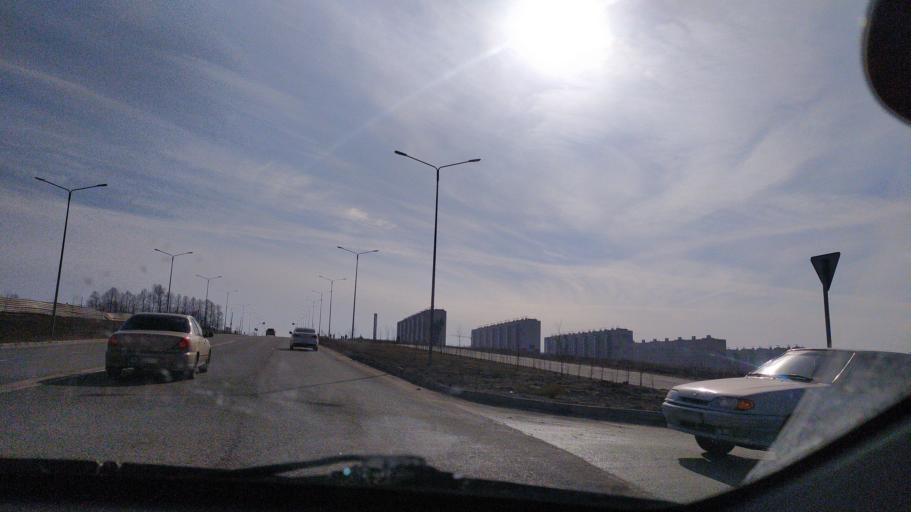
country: RU
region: Chuvashia
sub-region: Cheboksarskiy Rayon
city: Cheboksary
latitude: 56.1160
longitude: 47.2131
